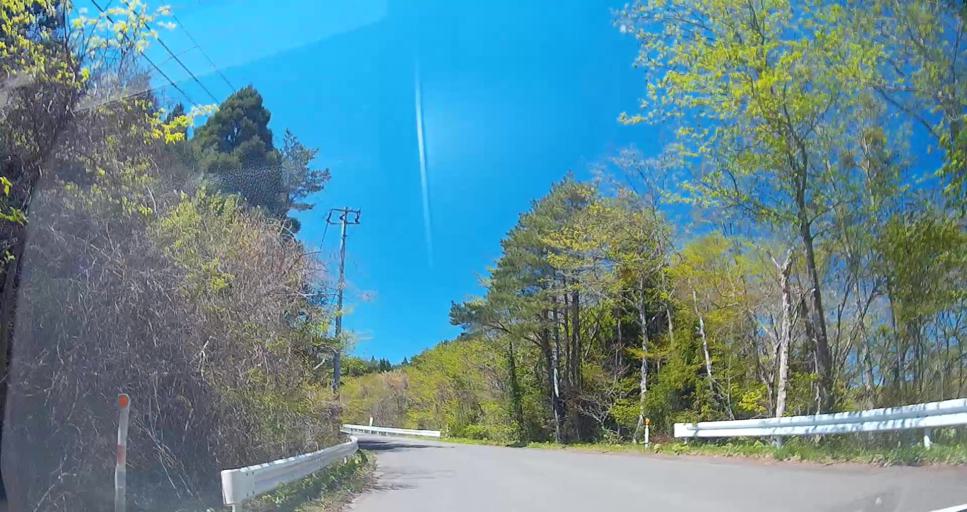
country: JP
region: Aomori
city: Mutsu
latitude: 41.2484
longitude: 141.3953
